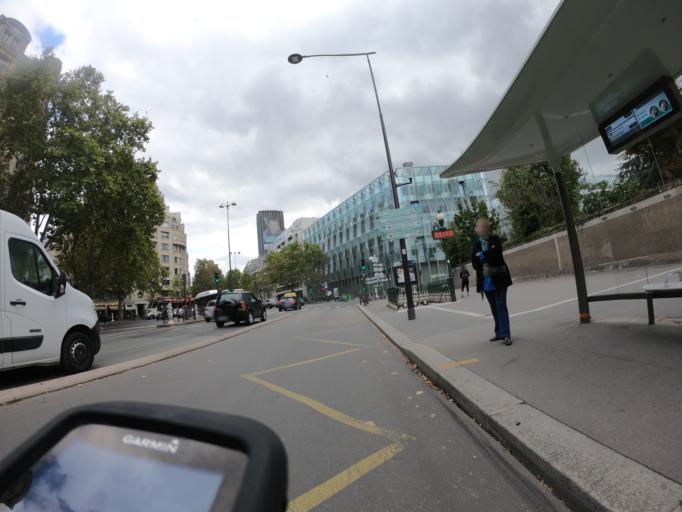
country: FR
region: Ile-de-France
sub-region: Departement des Hauts-de-Seine
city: Montrouge
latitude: 48.8472
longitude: 2.3163
